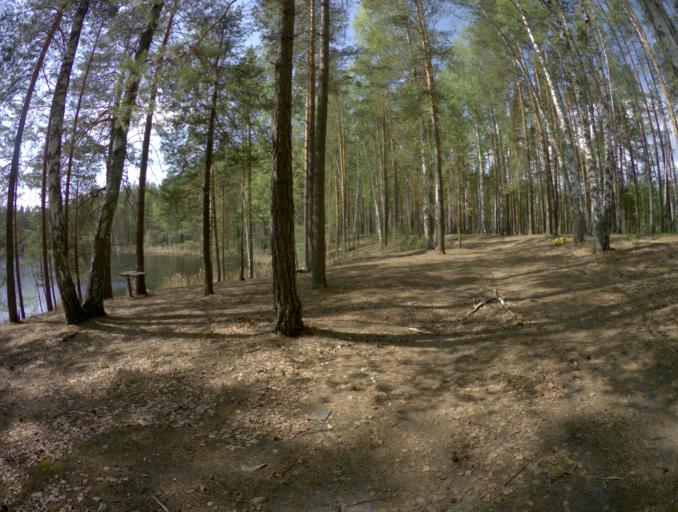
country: RU
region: Ivanovo
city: Talitsy
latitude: 56.4745
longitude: 42.1864
